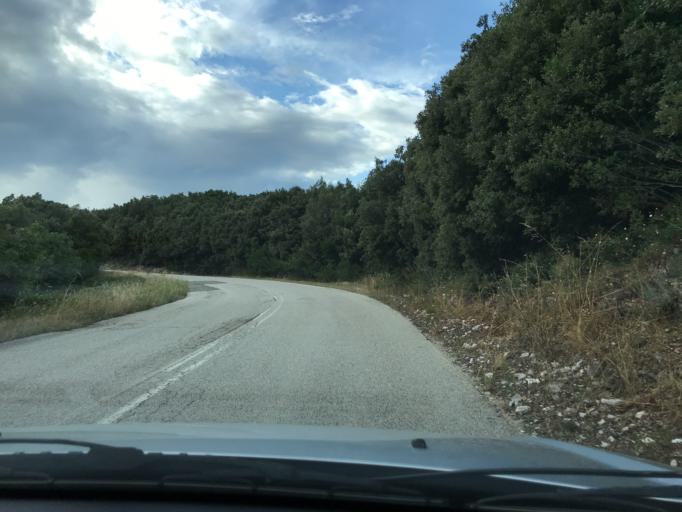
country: IT
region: Umbria
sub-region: Provincia di Terni
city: Montecchio
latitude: 42.6896
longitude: 12.2945
